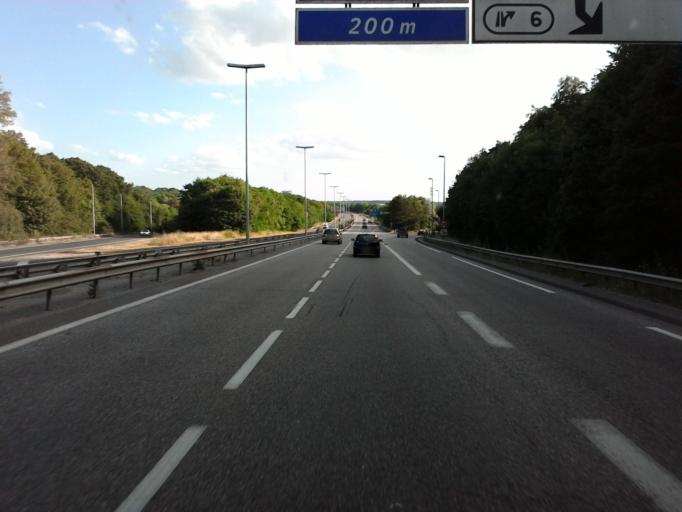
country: FR
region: Lorraine
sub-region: Departement de Meurthe-et-Moselle
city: Richardmenil
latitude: 48.6113
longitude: 6.1766
